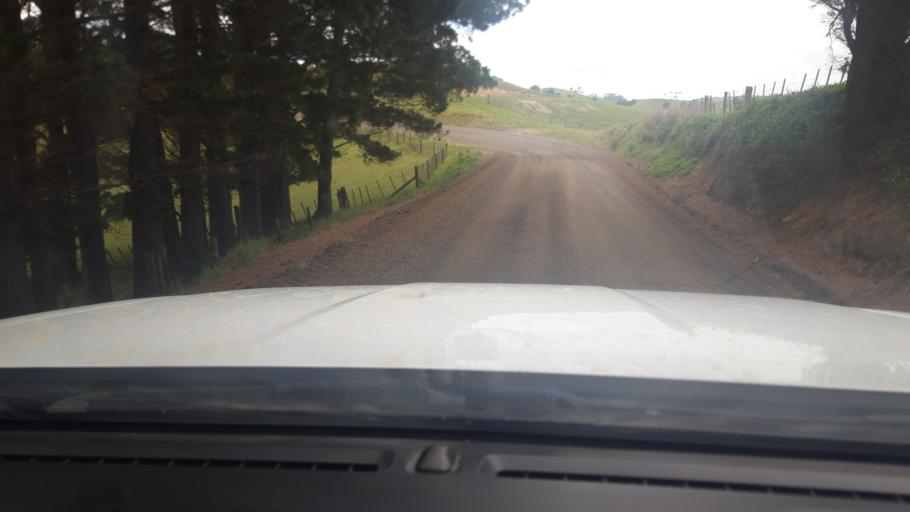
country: NZ
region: Northland
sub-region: Far North District
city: Kaitaia
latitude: -35.0776
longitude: 173.3217
